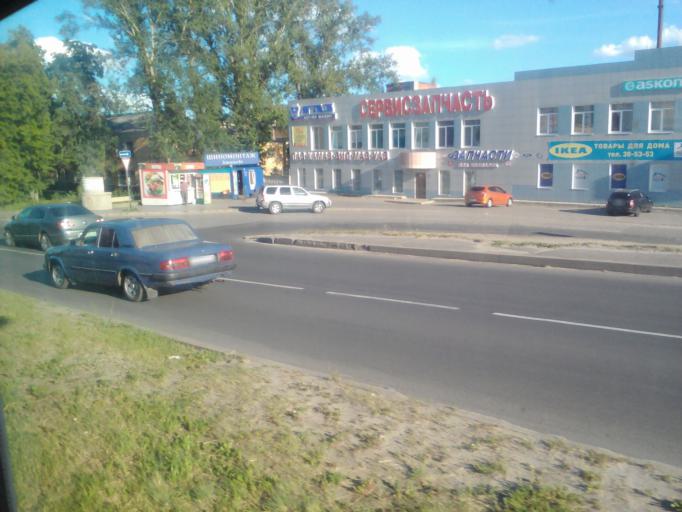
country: RU
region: Kursk
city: Kursk
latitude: 51.7047
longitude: 36.1682
